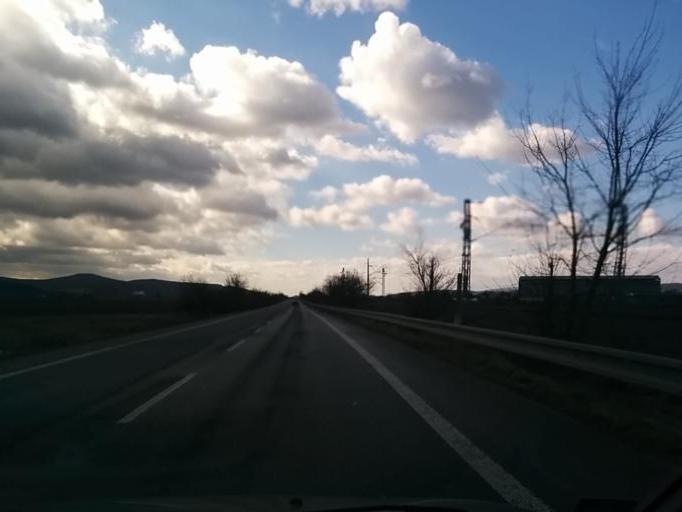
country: SK
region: Trenciansky
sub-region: Okres Trencin
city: Trencin
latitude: 48.8592
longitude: 17.9492
